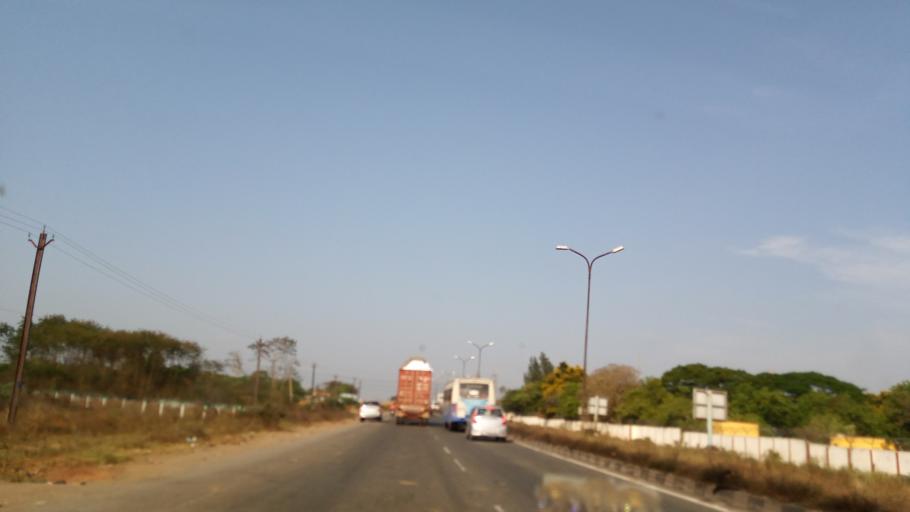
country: IN
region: Tamil Nadu
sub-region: Kancheepuram
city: Sriperumbudur
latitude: 12.9833
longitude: 79.9719
